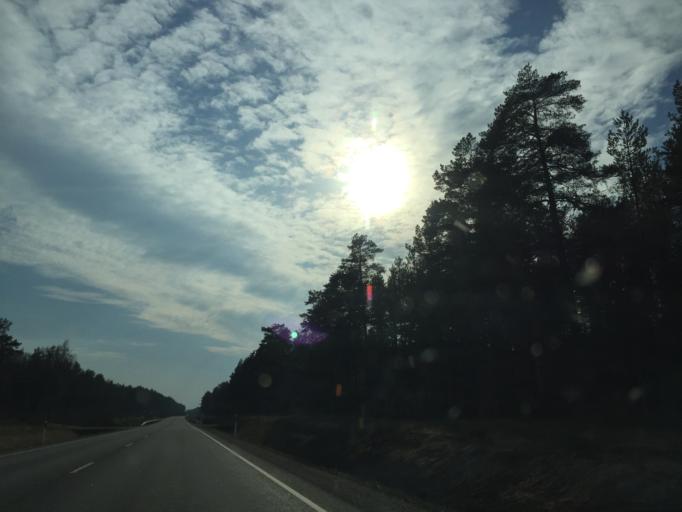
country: EE
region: Jogevamaa
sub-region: Mustvee linn
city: Mustvee
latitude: 58.9724
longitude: 27.1250
